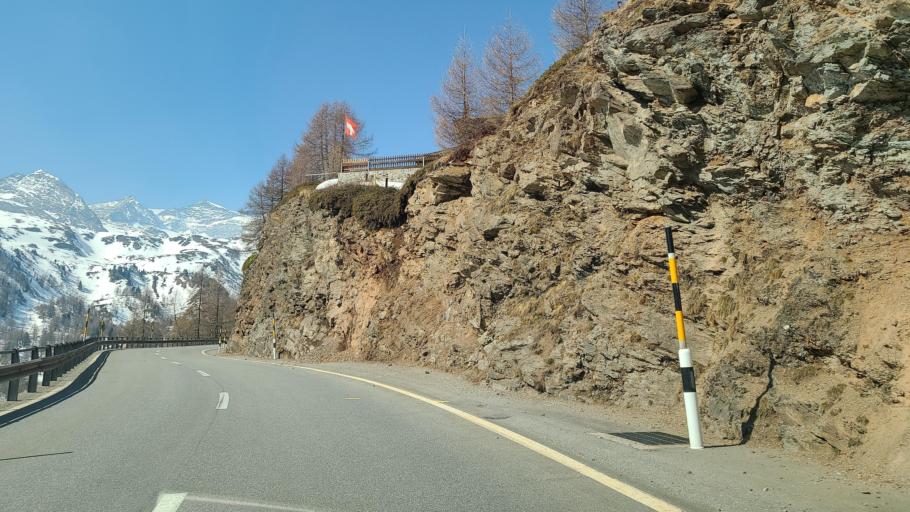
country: CH
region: Grisons
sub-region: Bernina District
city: Poschiavo
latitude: 46.4081
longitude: 10.0532
